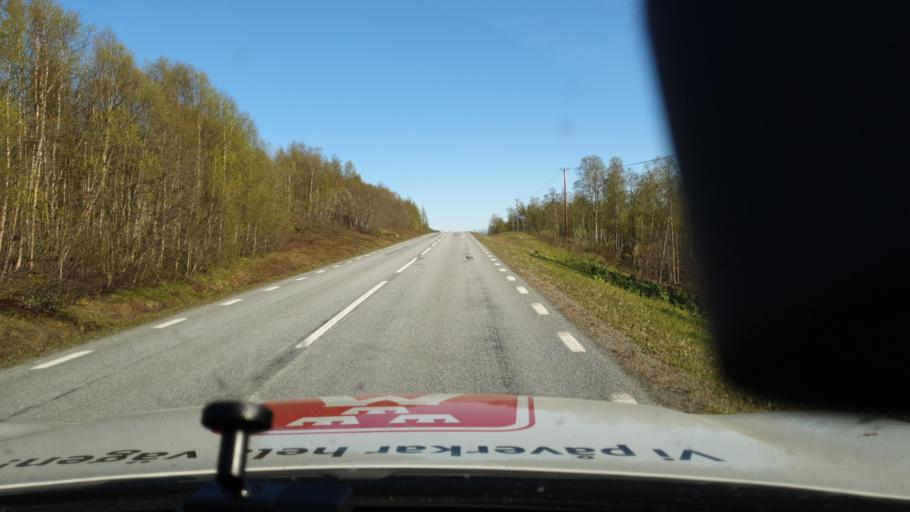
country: NO
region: Nordland
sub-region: Rana
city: Mo i Rana
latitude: 65.8481
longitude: 15.0378
